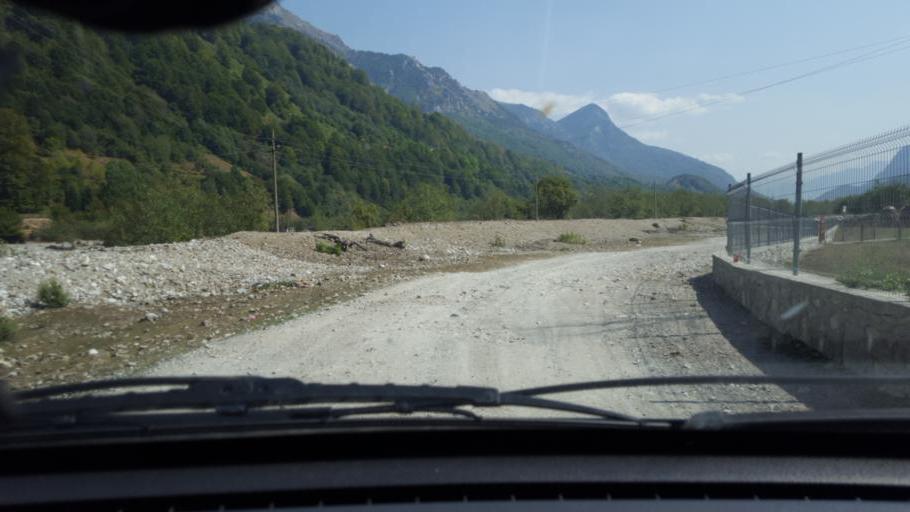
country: ME
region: Andrijevica
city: Andrijevica
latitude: 42.5936
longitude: 19.6805
